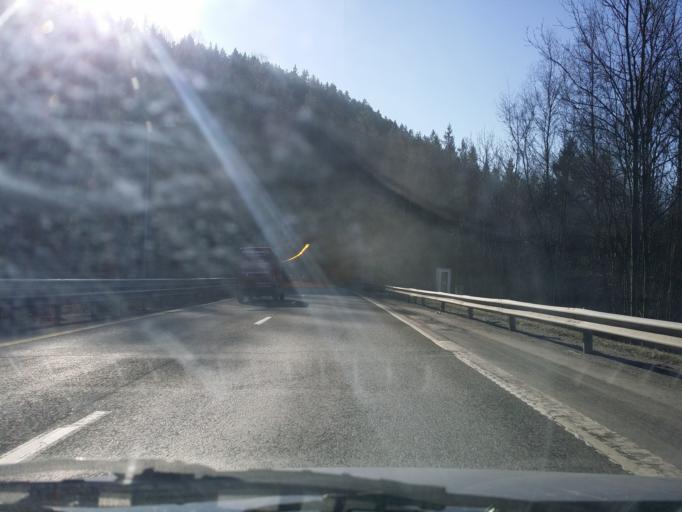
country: NO
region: Buskerud
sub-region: Lier
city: Tranby
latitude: 59.7961
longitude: 10.2677
